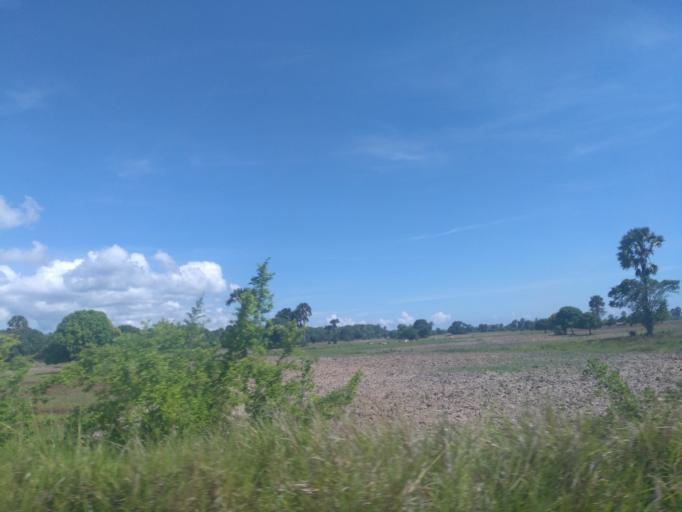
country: TZ
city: Kiwengwa
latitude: -5.9940
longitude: 39.3390
